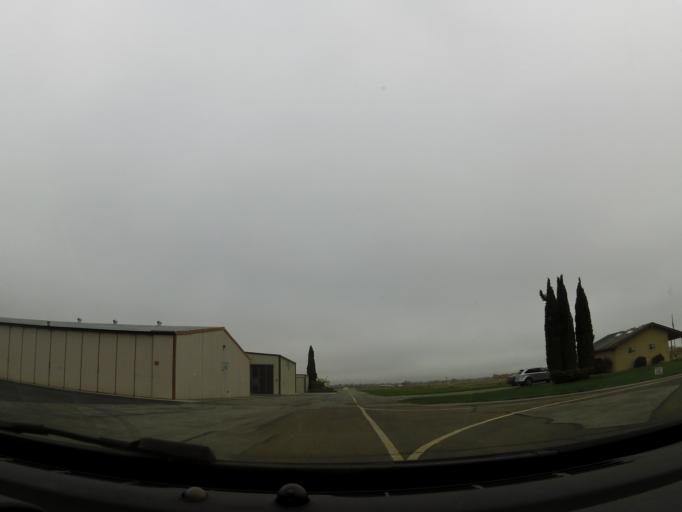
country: US
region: California
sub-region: Santa Clara County
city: Gilroy
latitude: 36.9529
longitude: -121.4677
